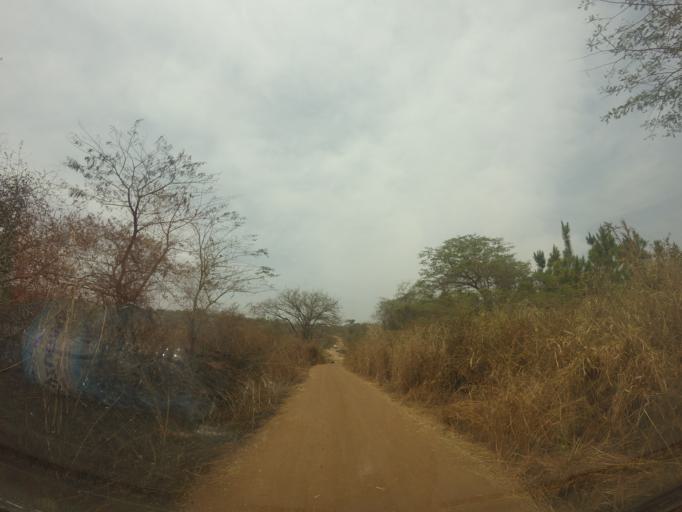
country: UG
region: Northern Region
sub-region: Nebbi District
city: Nebbi
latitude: 2.6294
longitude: 31.0369
